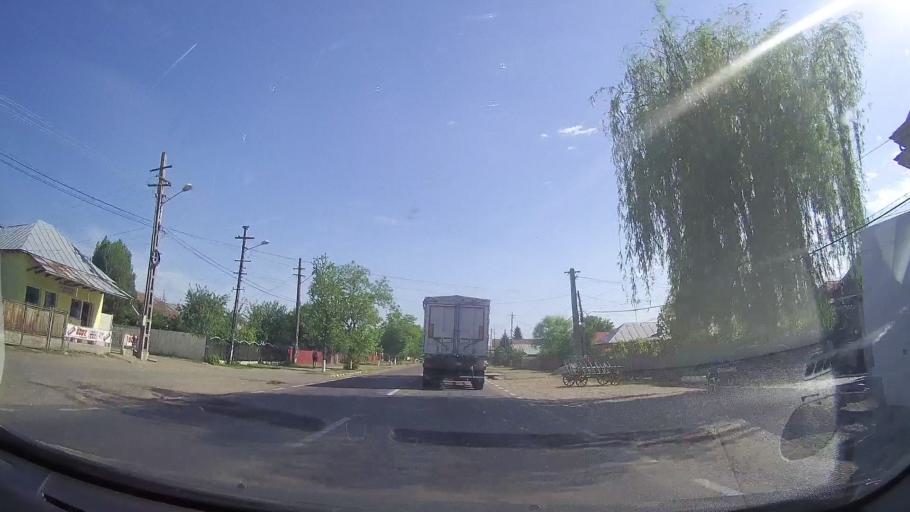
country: RO
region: Prahova
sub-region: Comuna Lipanesti
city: Lipanesti
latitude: 45.0532
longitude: 26.0198
